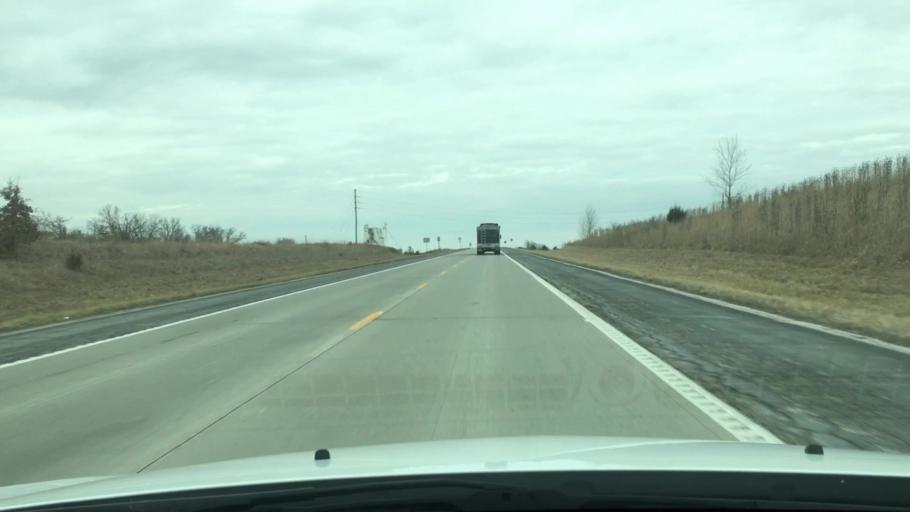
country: US
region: Missouri
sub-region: Audrain County
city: Mexico
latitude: 39.1519
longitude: -91.8434
